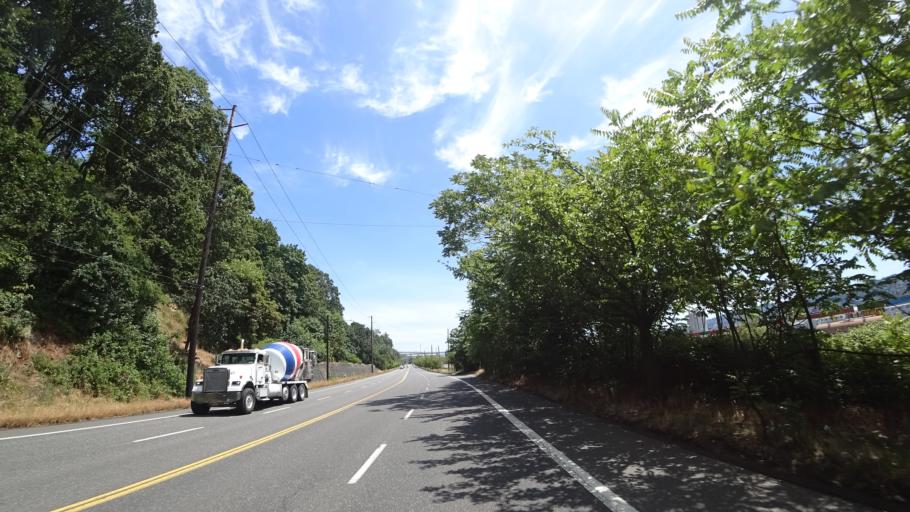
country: US
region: Oregon
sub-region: Multnomah County
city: Portland
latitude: 45.5514
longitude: -122.6894
